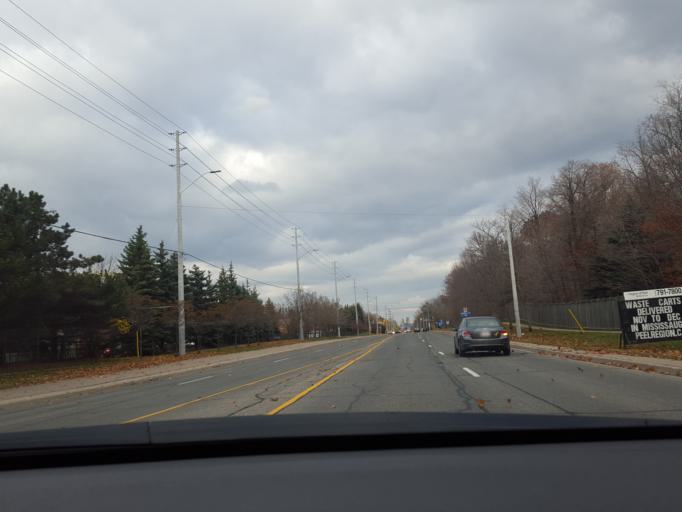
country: CA
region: Ontario
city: Mississauga
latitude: 43.5339
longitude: -79.7027
